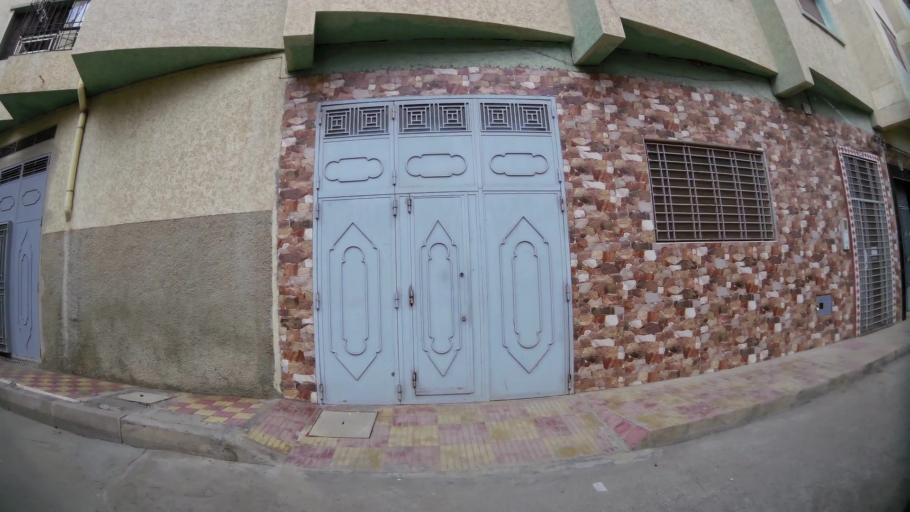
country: MA
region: Oriental
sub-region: Nador
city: Nador
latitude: 35.1637
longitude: -2.9308
